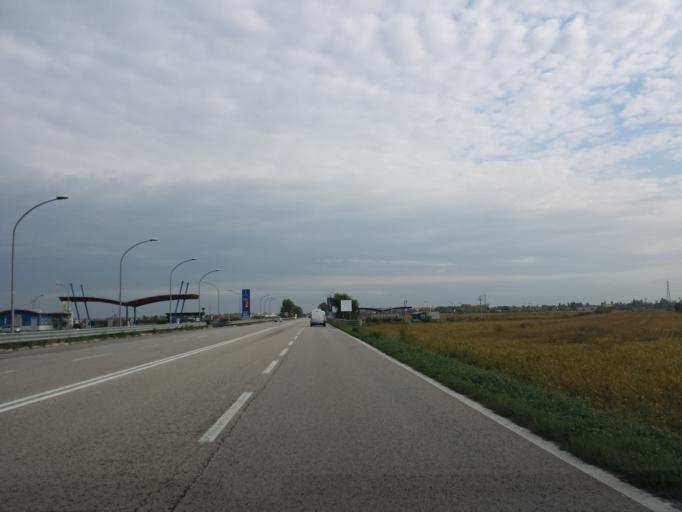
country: IT
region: Veneto
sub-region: Provincia di Padova
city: Boara Pisani
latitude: 45.0995
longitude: 11.7924
